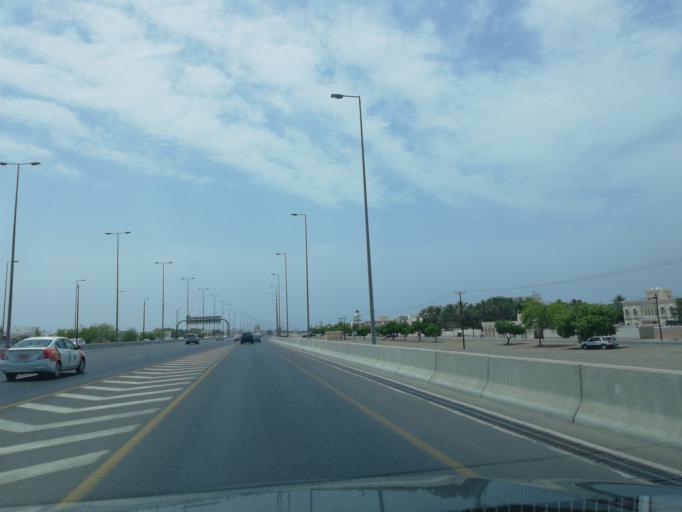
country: OM
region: Muhafazat Masqat
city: As Sib al Jadidah
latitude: 23.6665
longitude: 58.1588
